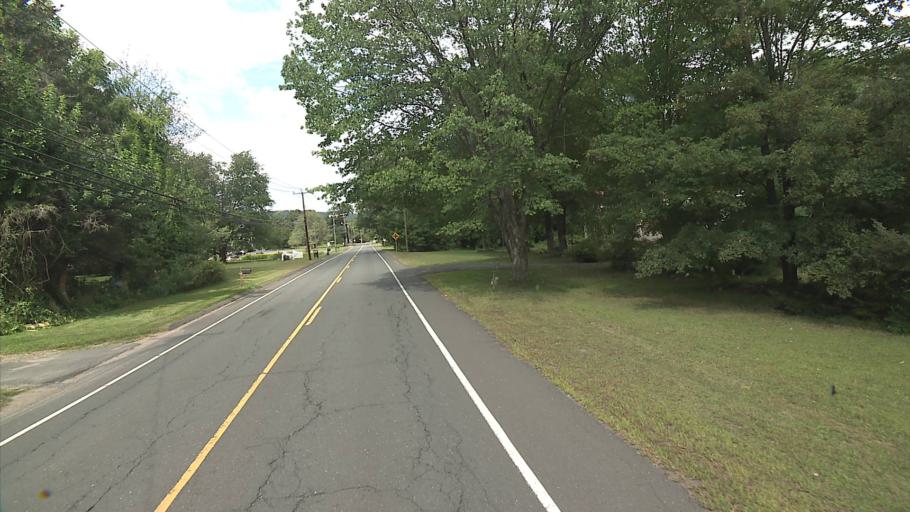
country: US
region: Connecticut
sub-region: Hartford County
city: Salmon Brook
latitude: 41.9753
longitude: -72.8106
